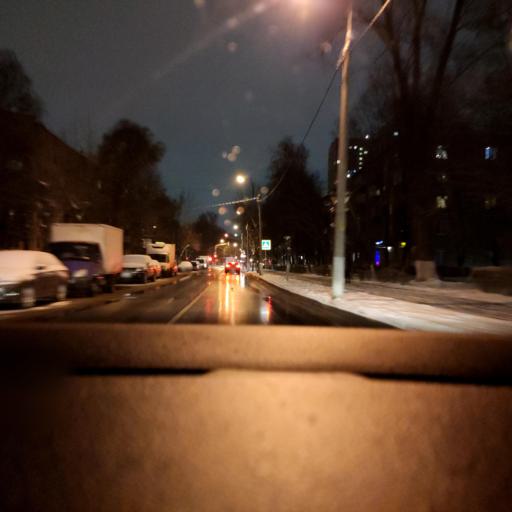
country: RU
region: Moskovskaya
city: Reutov
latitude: 55.7630
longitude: 37.8631
